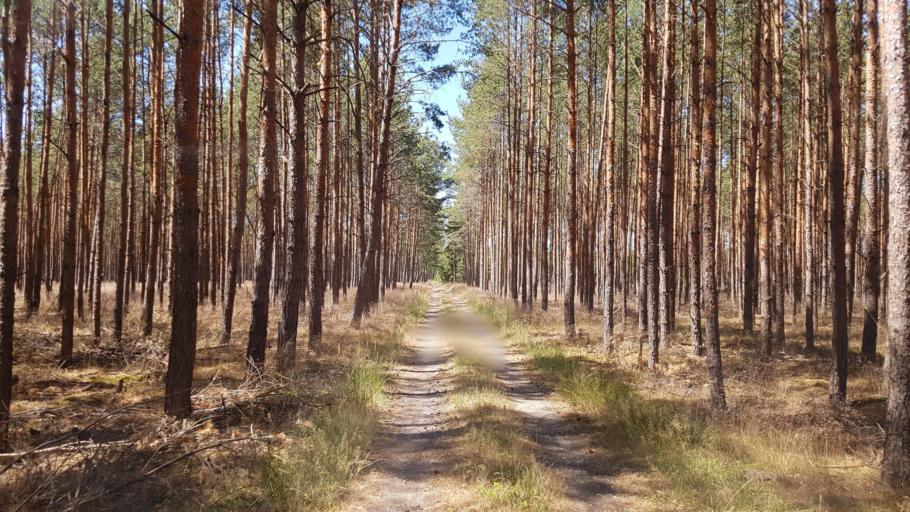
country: DE
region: Brandenburg
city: Treuenbrietzen
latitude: 52.0476
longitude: 12.8376
